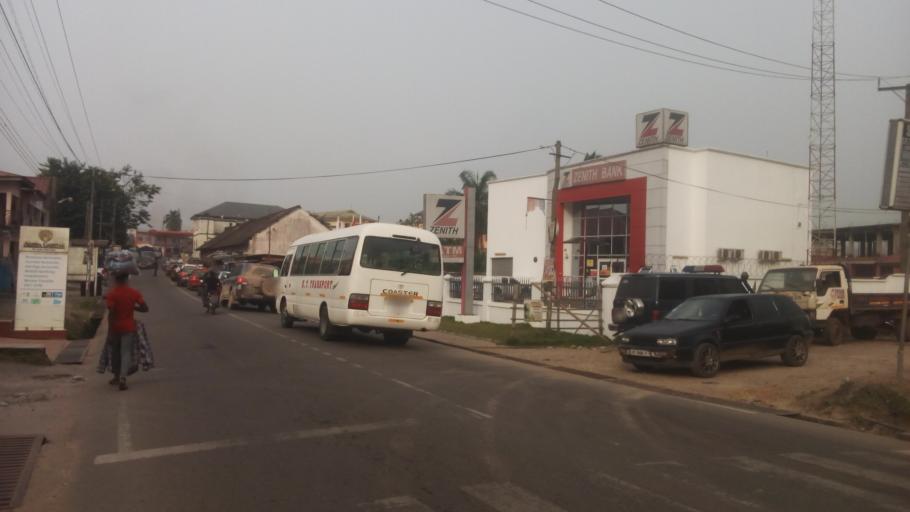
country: GH
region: Western
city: Tarkwa
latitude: 5.3033
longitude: -1.9924
